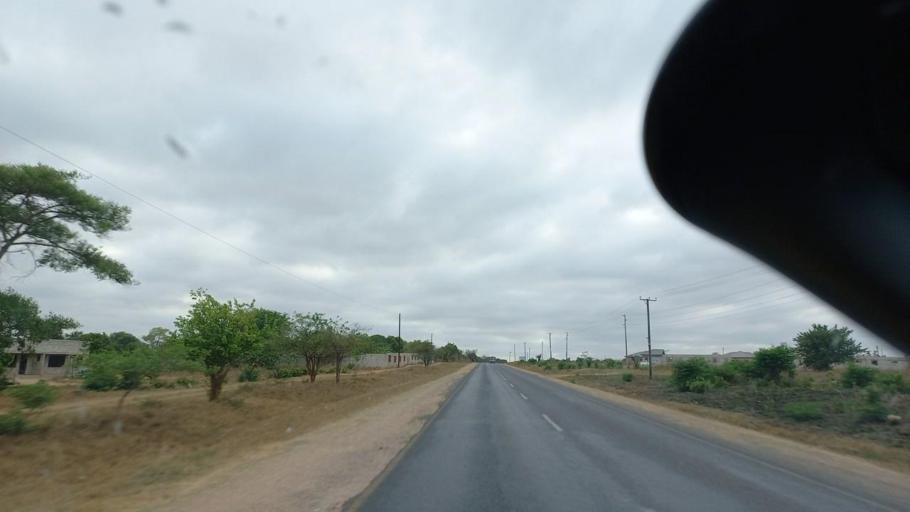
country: ZM
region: Lusaka
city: Chongwe
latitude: -15.3402
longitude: 28.6327
